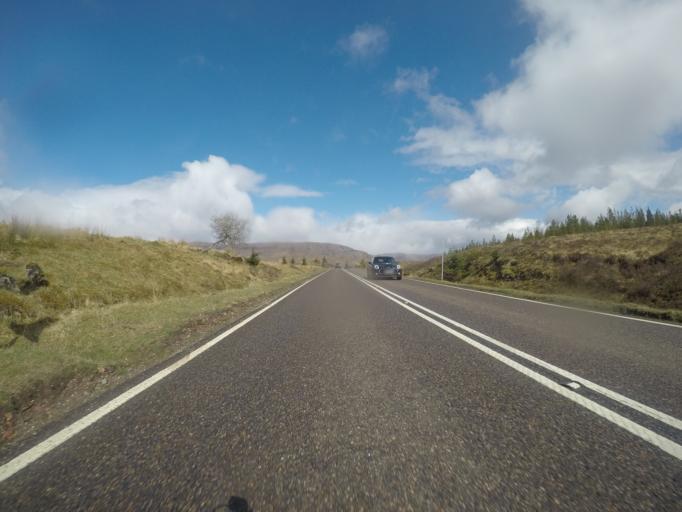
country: GB
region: Scotland
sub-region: Highland
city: Spean Bridge
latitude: 57.0949
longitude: -4.9941
